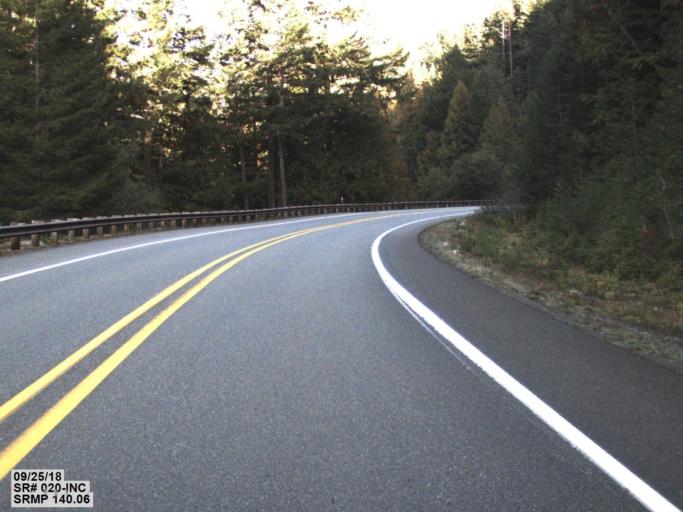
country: US
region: Washington
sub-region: Snohomish County
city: Darrington
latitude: 48.7052
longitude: -120.9437
